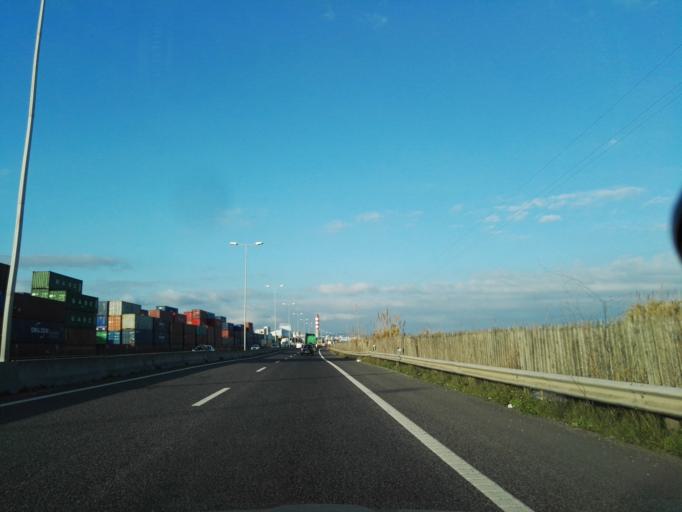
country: PT
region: Lisbon
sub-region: Loures
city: Sao Joao da Talha
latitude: 38.8170
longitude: -9.0871
